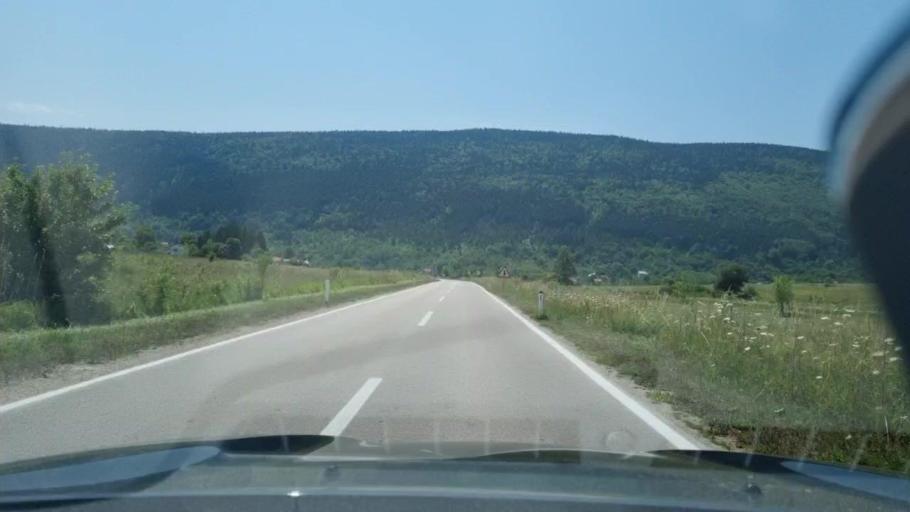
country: BA
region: Federation of Bosnia and Herzegovina
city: Orasac
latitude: 44.5256
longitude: 16.3453
